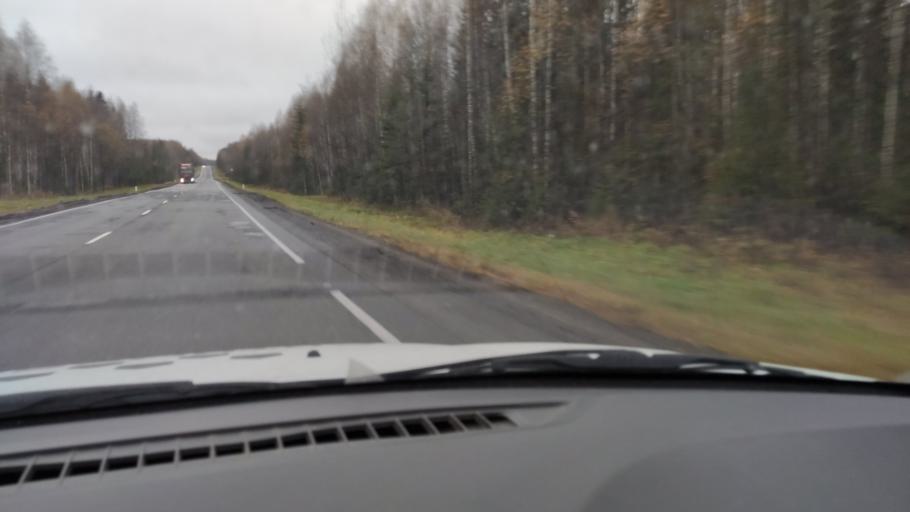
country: RU
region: Kirov
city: Chernaya Kholunitsa
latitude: 58.7716
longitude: 51.9518
